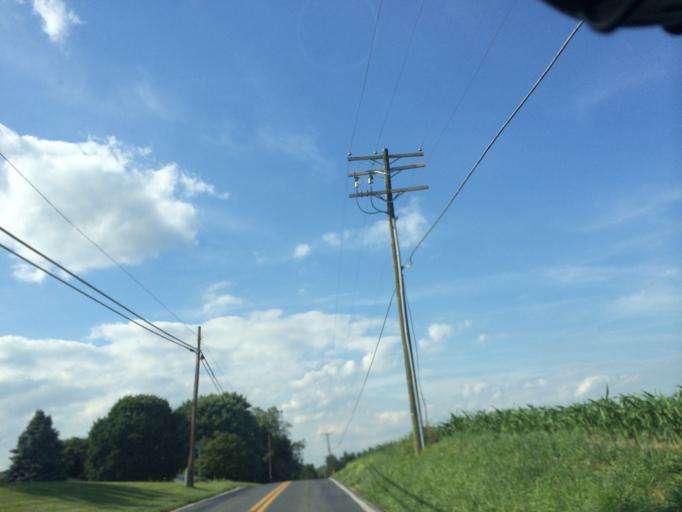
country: US
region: Maryland
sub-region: Carroll County
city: Sykesville
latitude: 39.3236
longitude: -77.0616
